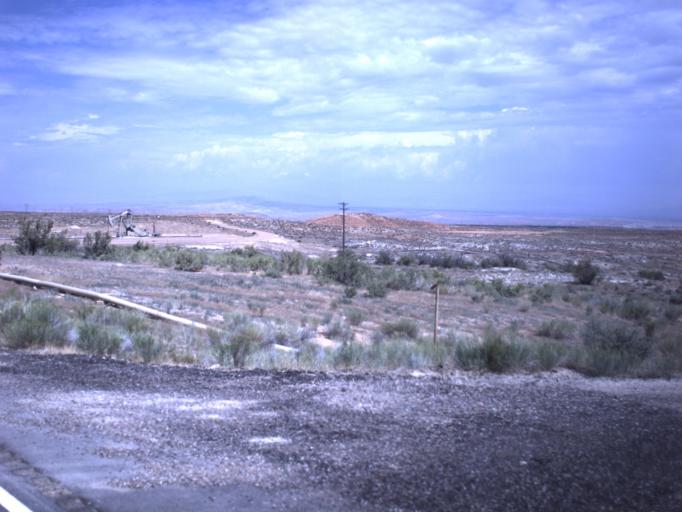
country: US
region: Utah
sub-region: Uintah County
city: Naples
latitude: 40.2101
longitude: -109.3696
